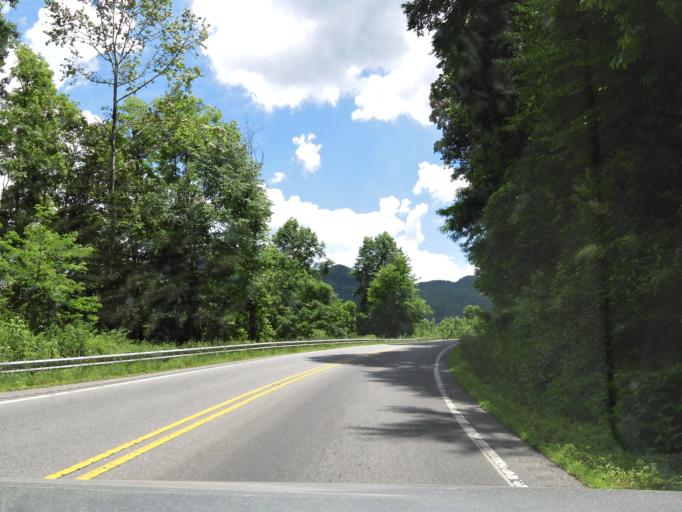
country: US
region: North Carolina
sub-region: Graham County
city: Robbinsville
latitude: 35.2727
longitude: -83.6909
